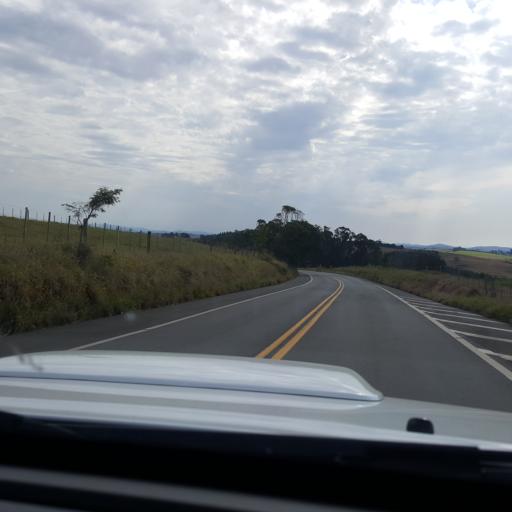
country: BR
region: Sao Paulo
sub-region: Itaporanga
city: Itaporanga
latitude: -23.7754
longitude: -49.4328
